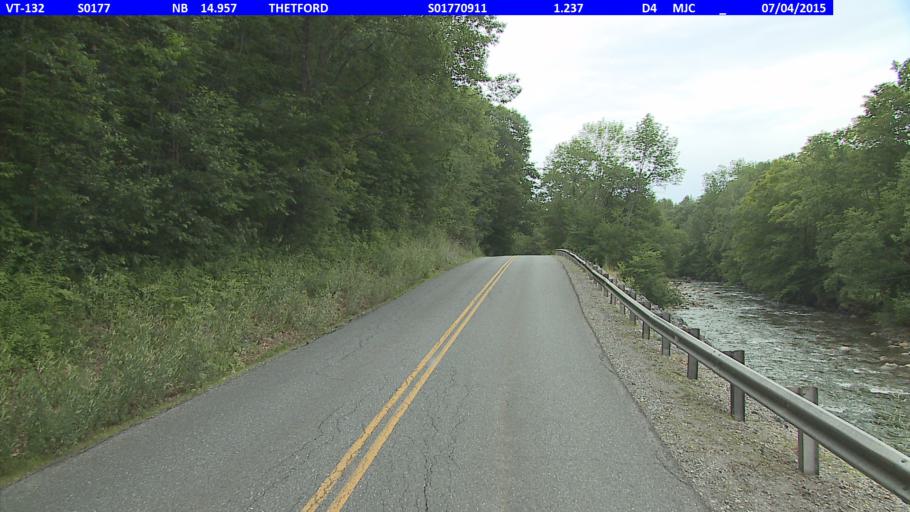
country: US
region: New Hampshire
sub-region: Grafton County
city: Hanover
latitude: 43.8327
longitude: -72.2991
